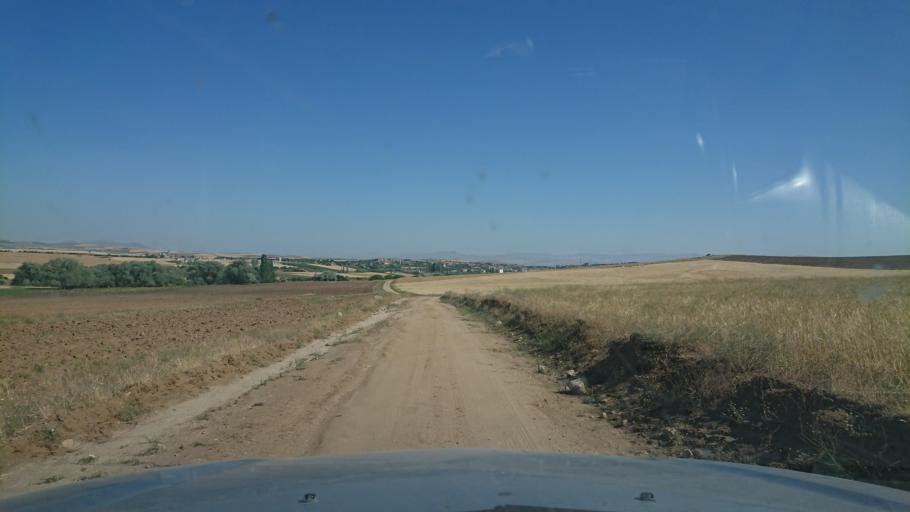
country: TR
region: Aksaray
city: Agacoren
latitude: 38.8496
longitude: 33.9160
